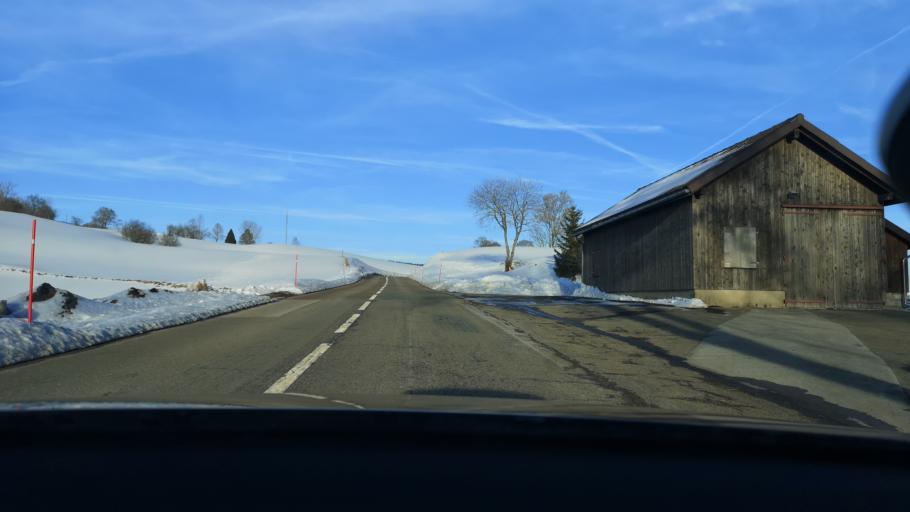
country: CH
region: Neuchatel
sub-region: Val-de-Travers District
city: Fleurier
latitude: 46.9104
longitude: 6.5019
